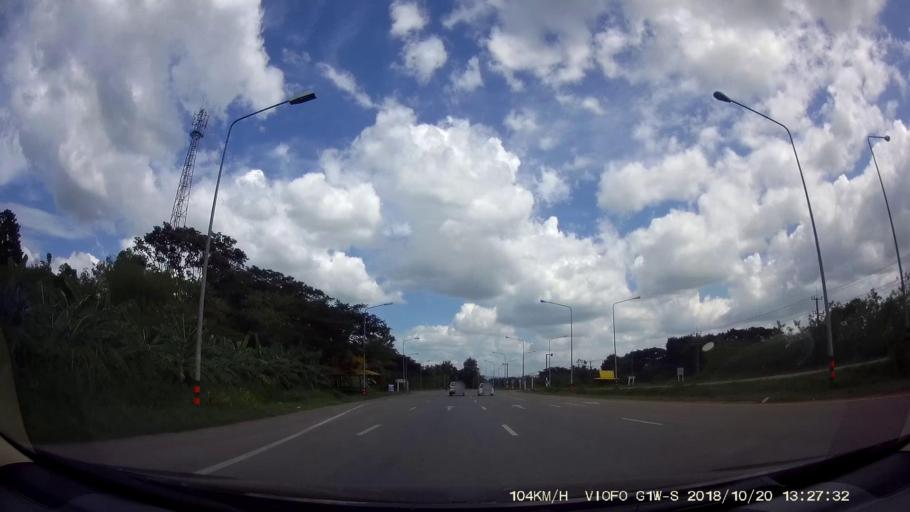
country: TH
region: Chaiyaphum
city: Khon San
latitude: 16.5925
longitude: 101.9619
